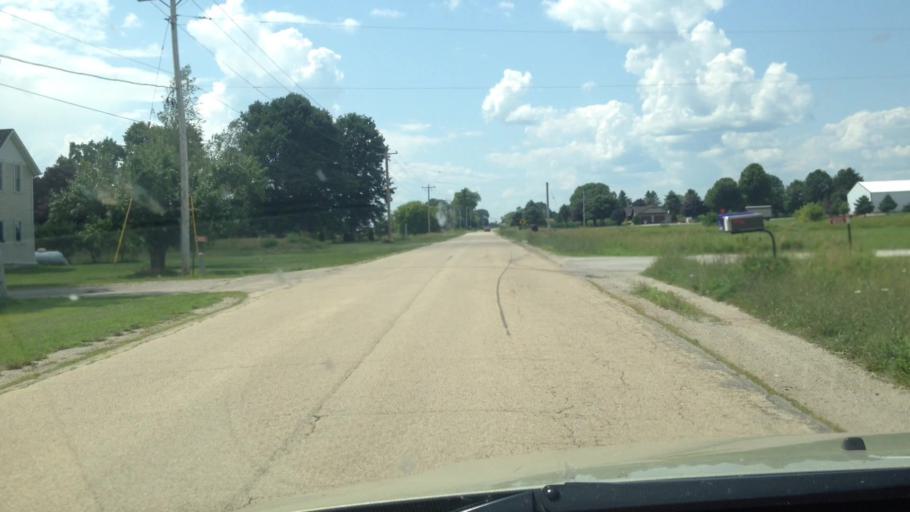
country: US
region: Wisconsin
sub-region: Brown County
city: Pulaski
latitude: 44.6567
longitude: -88.2560
